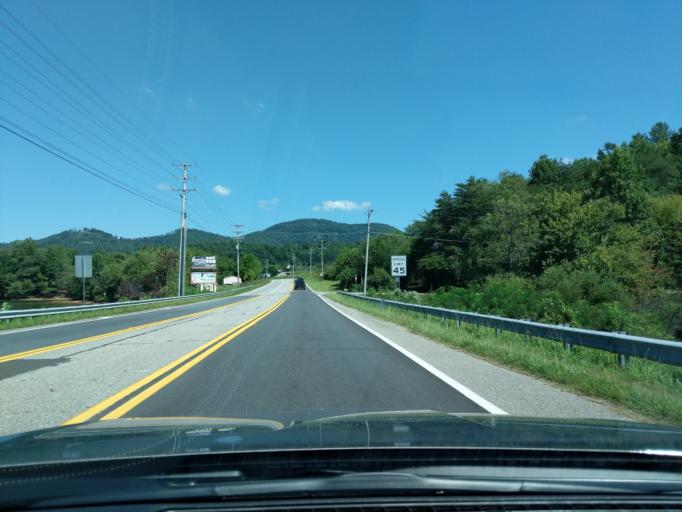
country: US
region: Georgia
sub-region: Towns County
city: Hiawassee
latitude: 34.9246
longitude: -83.7318
